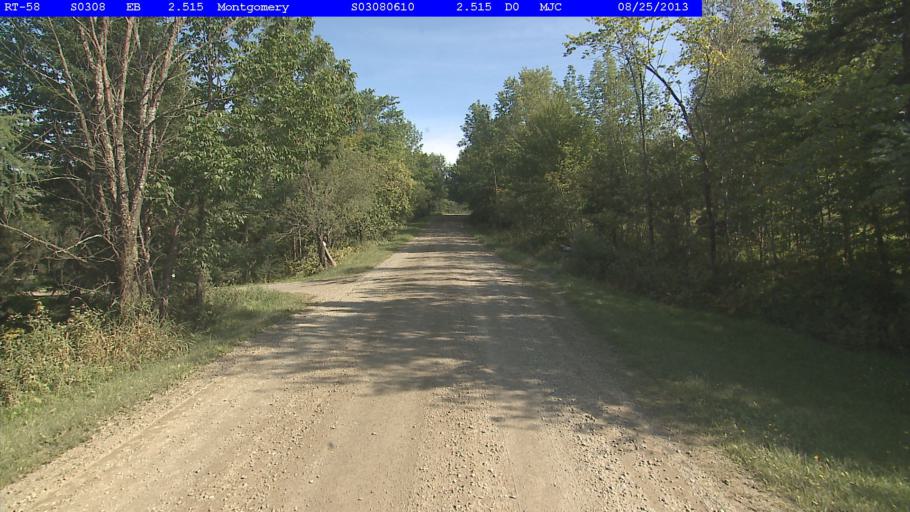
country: US
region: Vermont
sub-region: Franklin County
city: Richford
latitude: 44.8618
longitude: -72.5655
